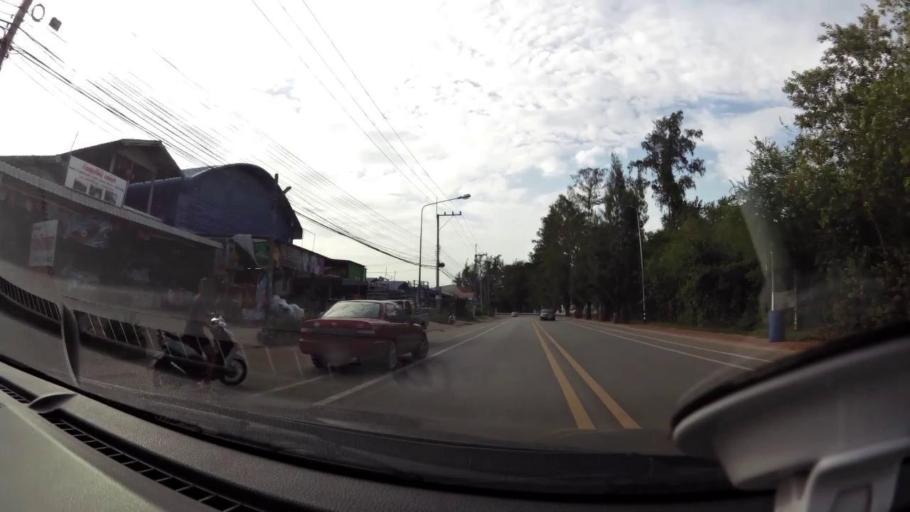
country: TH
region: Prachuap Khiri Khan
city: Hua Hin
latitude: 12.4648
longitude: 99.9741
